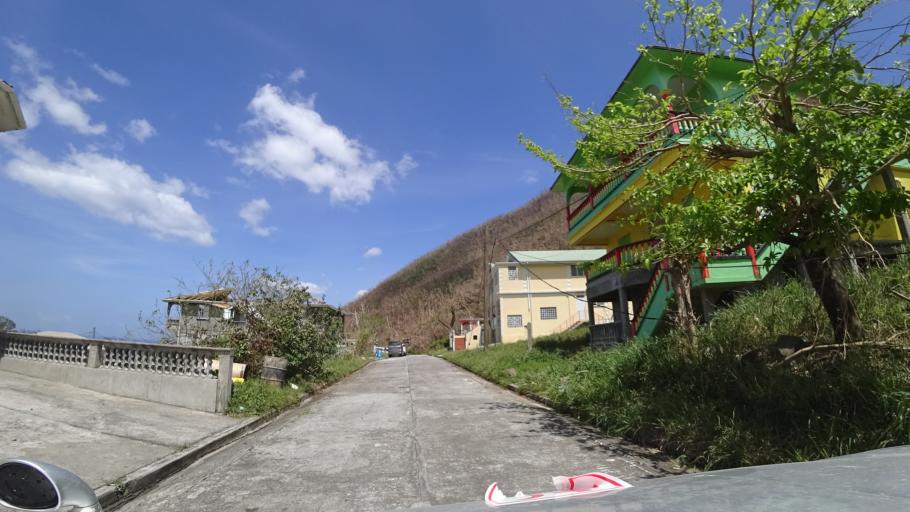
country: DM
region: Saint Luke
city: Pointe Michel
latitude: 15.2601
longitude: -61.3732
